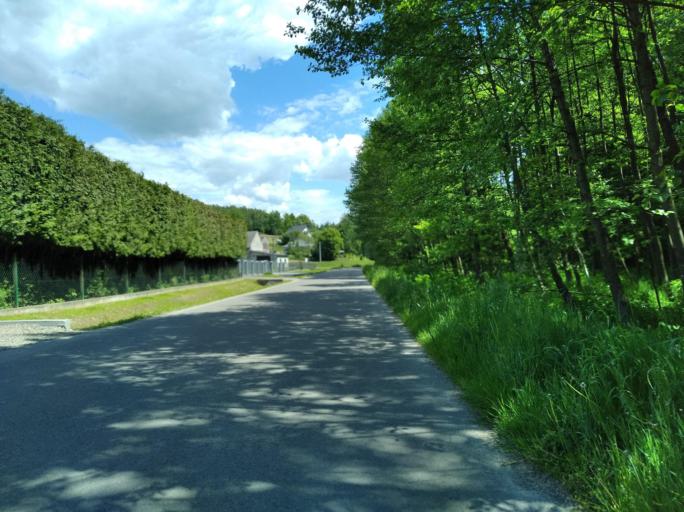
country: PL
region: Subcarpathian Voivodeship
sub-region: Powiat krosnienski
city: Leki
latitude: 49.7871
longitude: 21.6230
